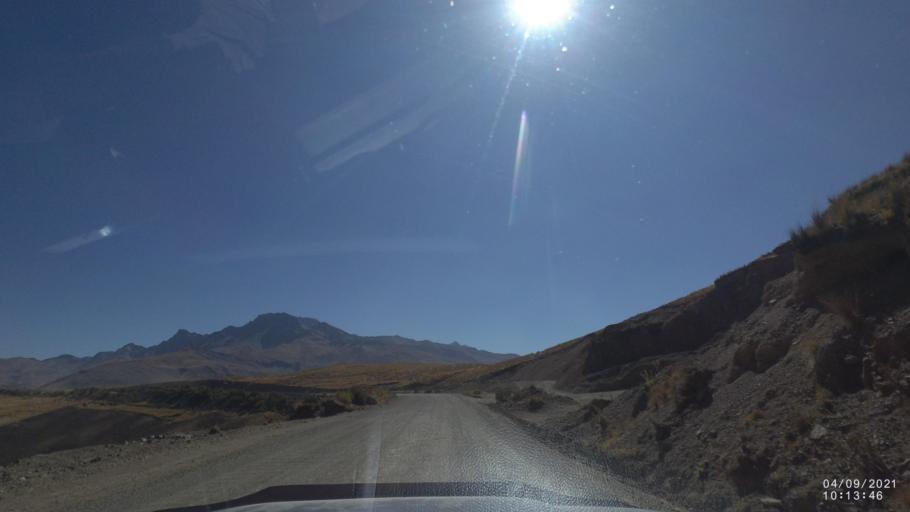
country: BO
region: Cochabamba
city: Sipe Sipe
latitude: -17.3347
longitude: -66.4064
